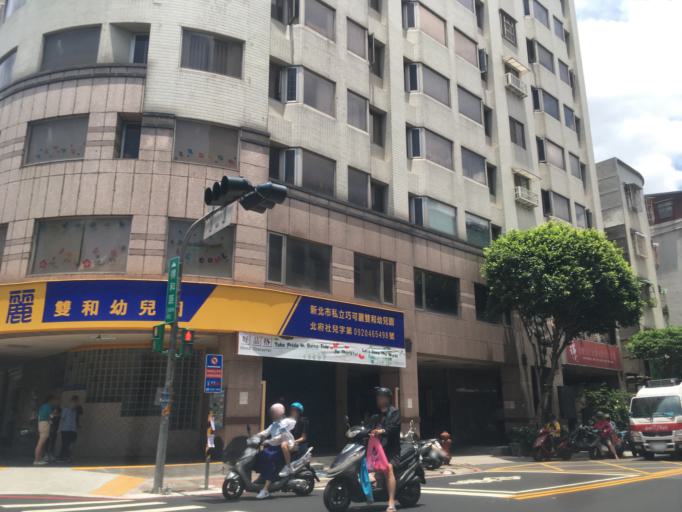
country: TW
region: Taipei
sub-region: Taipei
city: Banqiao
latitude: 25.0008
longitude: 121.5146
